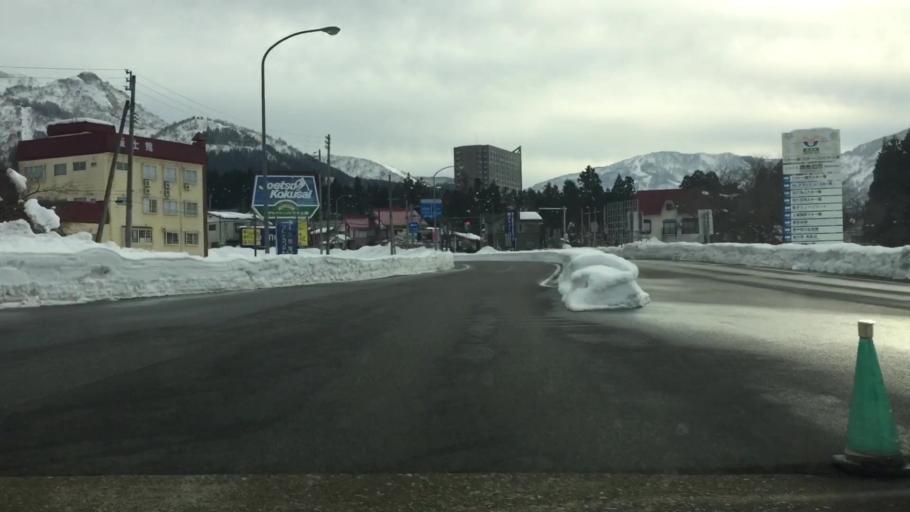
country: JP
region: Niigata
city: Shiozawa
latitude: 36.9930
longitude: 138.8214
